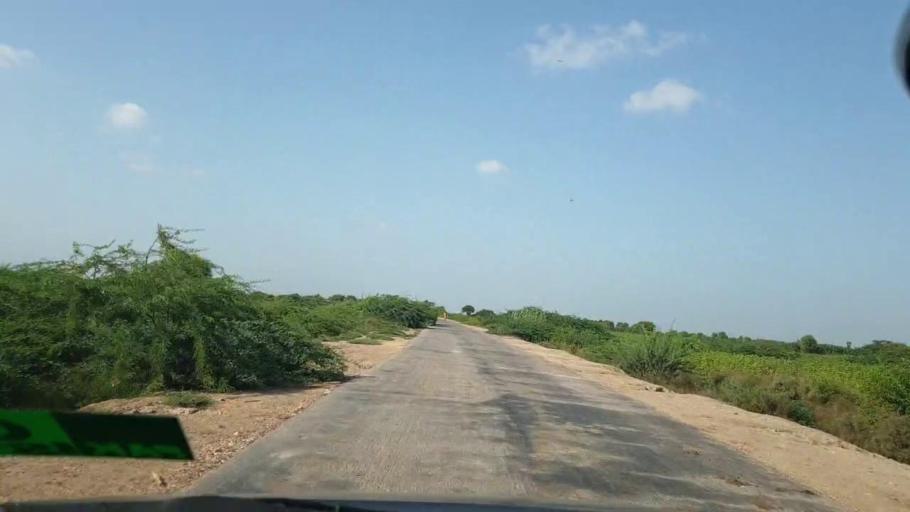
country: PK
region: Sindh
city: Tando Bago
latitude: 24.7166
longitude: 69.1937
